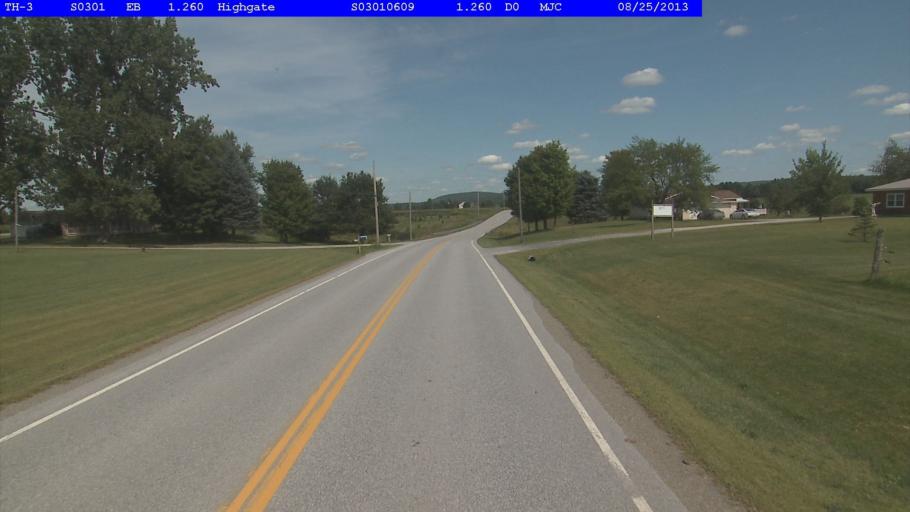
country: US
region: Vermont
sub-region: Franklin County
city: Swanton
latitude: 44.9572
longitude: -72.9949
